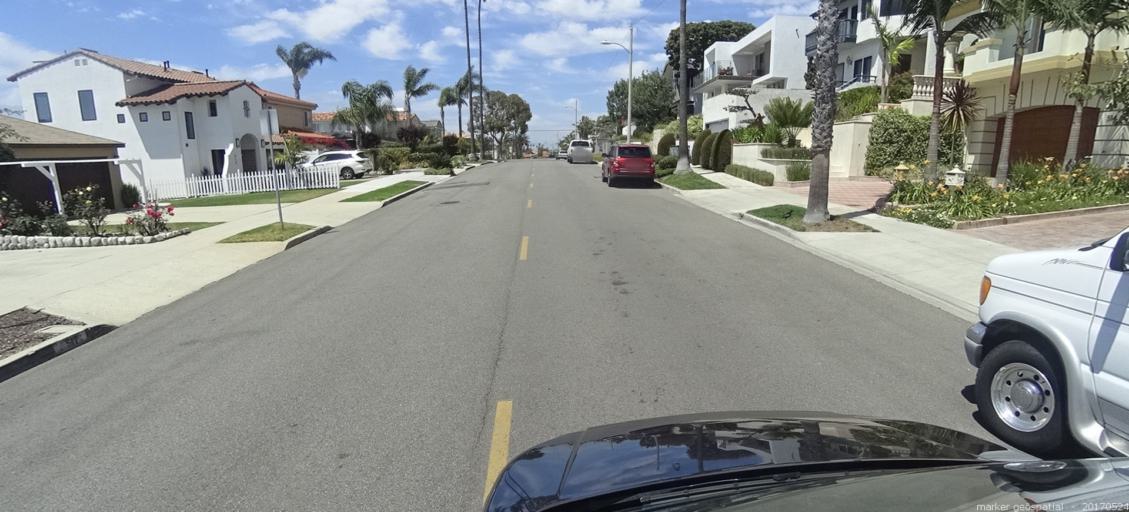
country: US
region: California
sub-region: Los Angeles County
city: Redondo Beach
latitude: 33.8334
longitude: -118.3832
